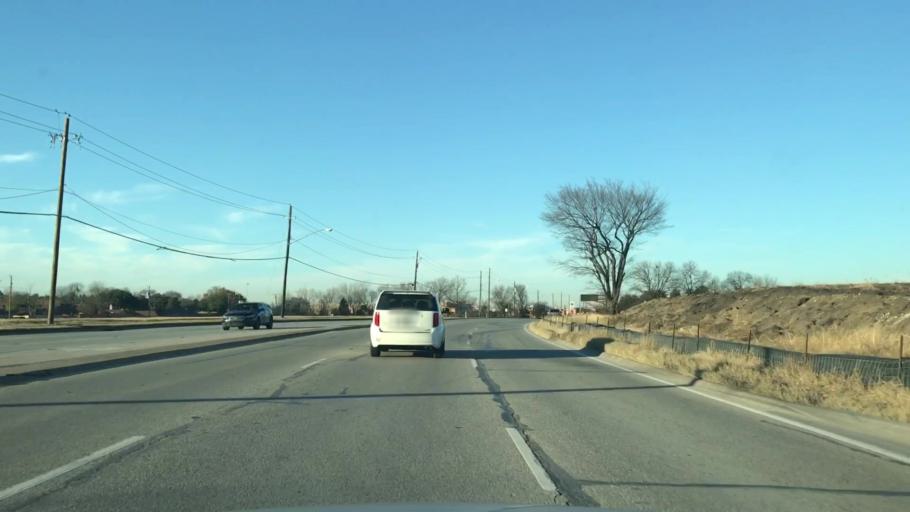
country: US
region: Texas
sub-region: Dallas County
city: Balch Springs
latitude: 32.7870
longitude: -96.6849
